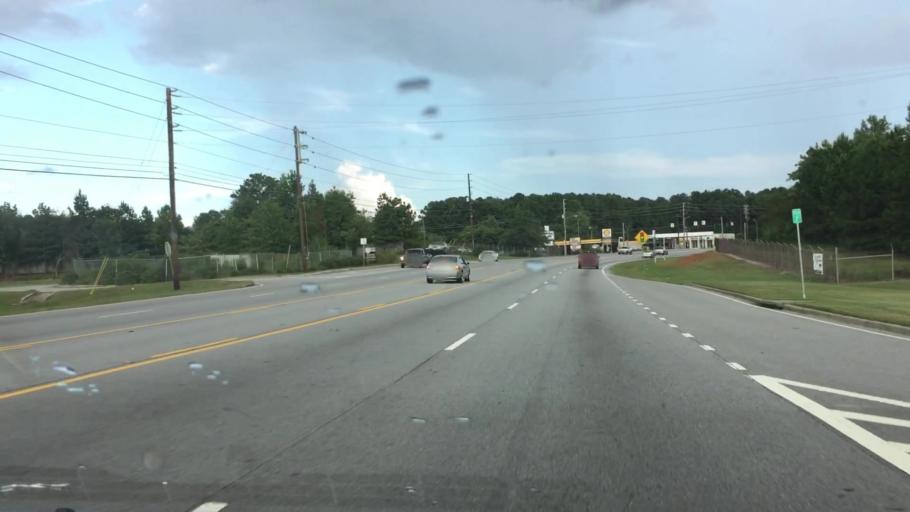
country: US
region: Georgia
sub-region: Clayton County
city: Riverdale
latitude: 33.5464
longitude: -84.4064
